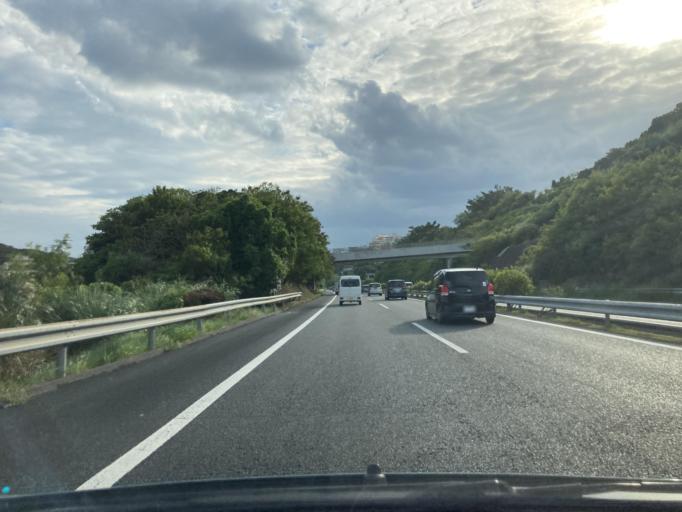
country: JP
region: Okinawa
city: Ginowan
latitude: 26.2725
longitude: 127.7779
